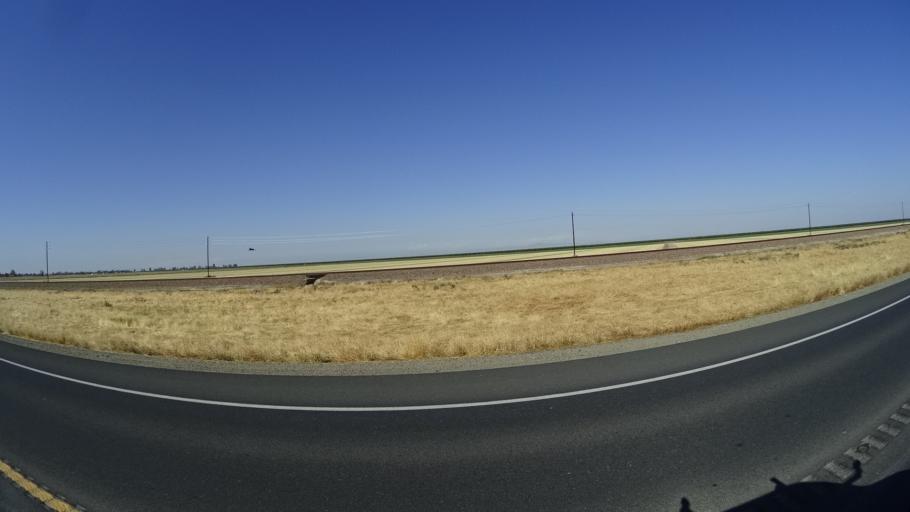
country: US
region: California
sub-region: Kings County
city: Corcoran
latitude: 36.1319
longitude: -119.5807
